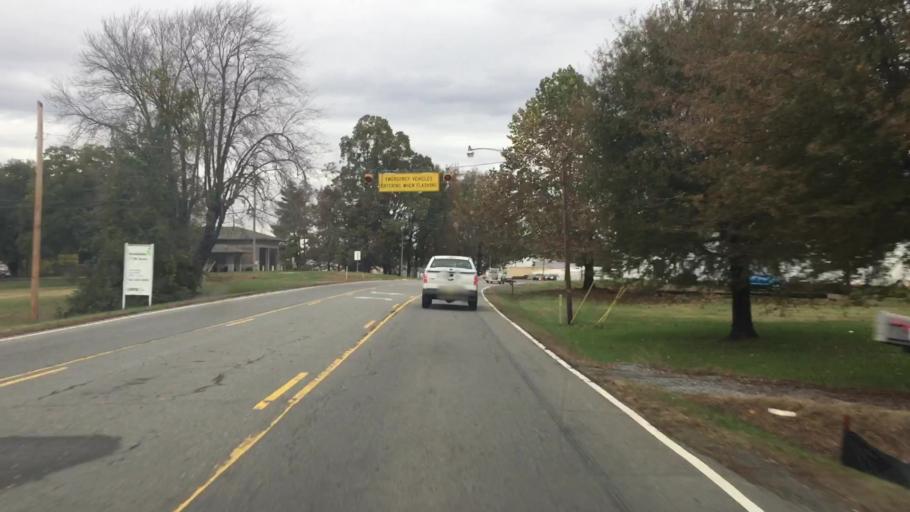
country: US
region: North Carolina
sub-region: Rockingham County
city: Reidsville
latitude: 36.3342
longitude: -79.6522
